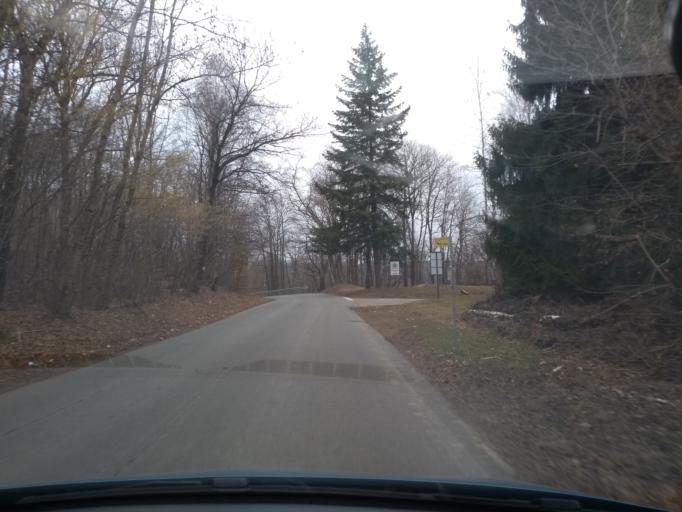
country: IT
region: Piedmont
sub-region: Provincia di Torino
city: Palazzo Canavese
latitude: 45.4817
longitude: 7.9737
